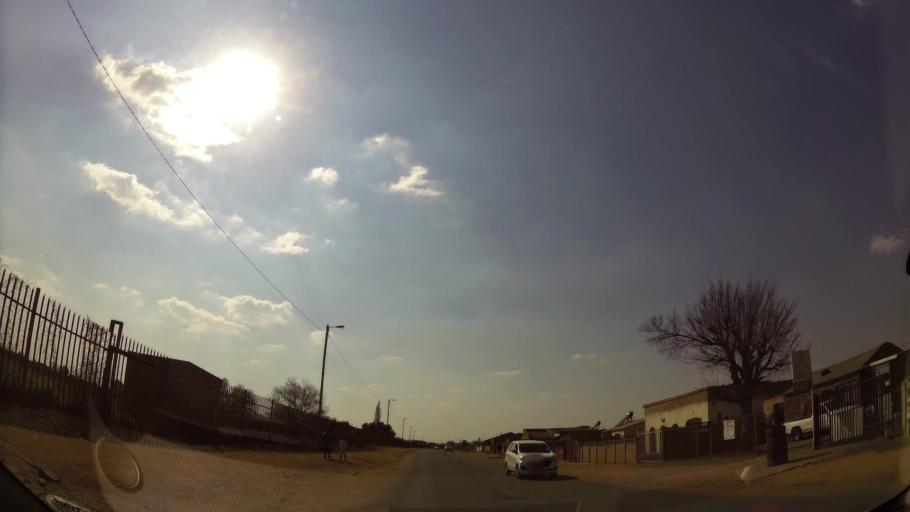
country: ZA
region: Gauteng
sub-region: Ekurhuleni Metropolitan Municipality
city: Benoni
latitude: -26.1469
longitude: 28.4083
